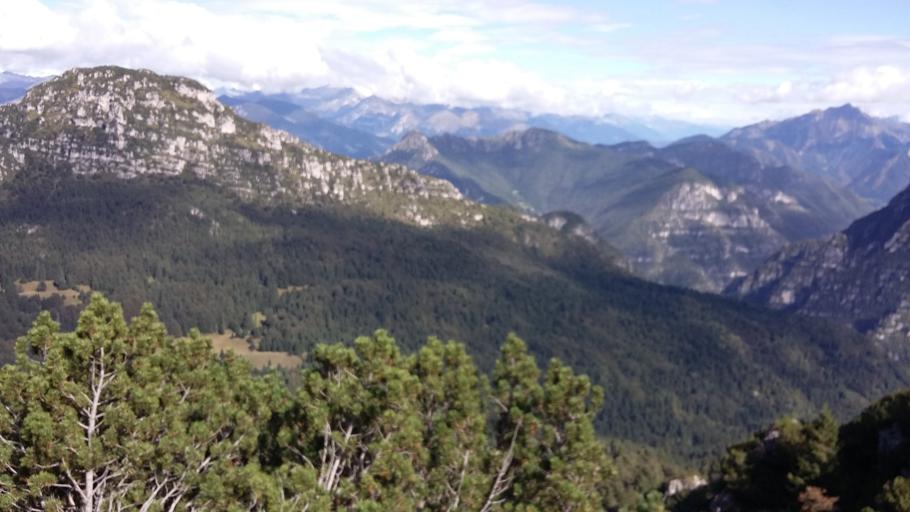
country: IT
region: Lombardy
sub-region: Provincia di Brescia
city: Magasa
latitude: 45.8036
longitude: 10.5989
